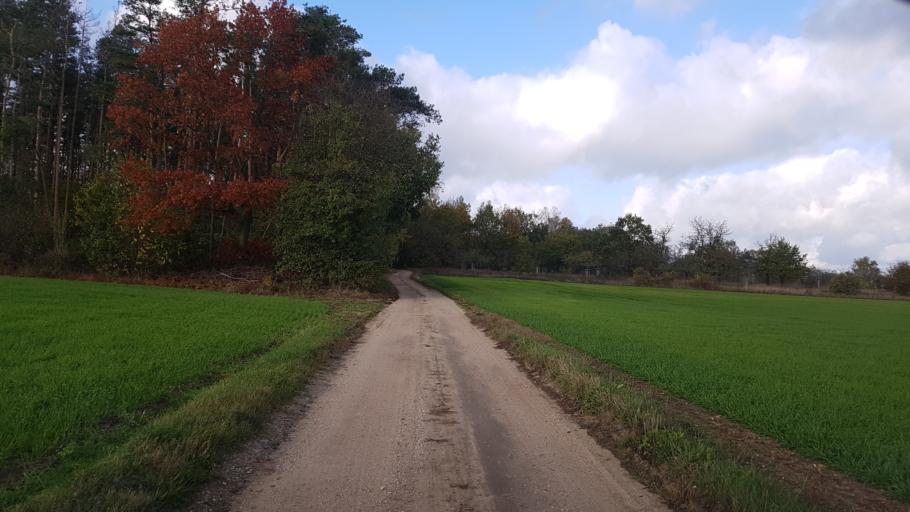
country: DE
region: Brandenburg
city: Doberlug-Kirchhain
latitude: 51.6330
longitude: 13.5356
